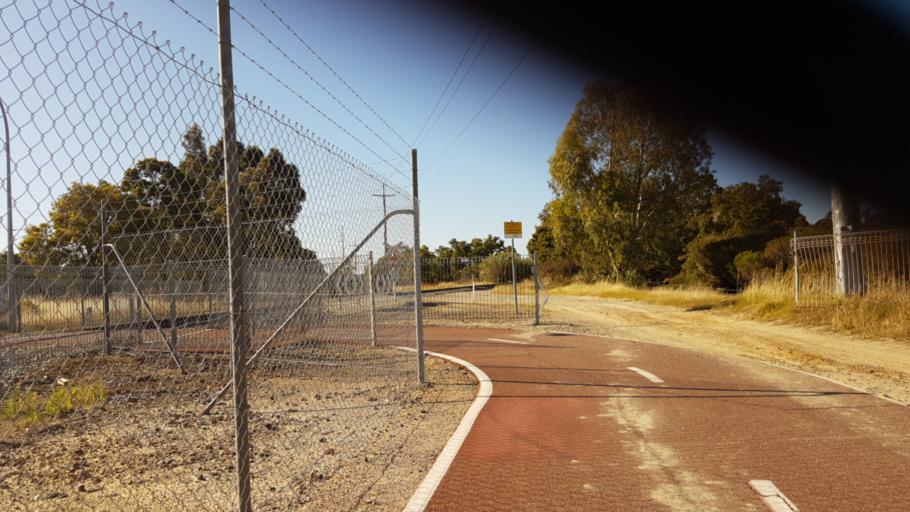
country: AU
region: Western Australia
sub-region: Gosnells
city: Kenwick
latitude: -32.0346
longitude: 115.9684
